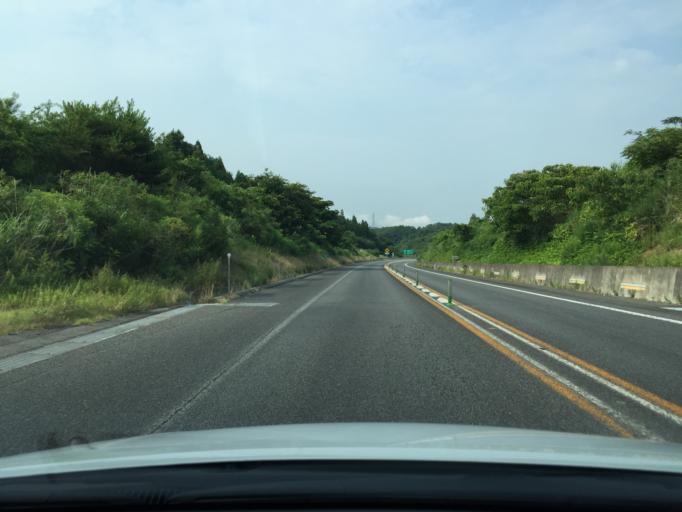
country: JP
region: Fukushima
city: Iwaki
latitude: 37.1013
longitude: 140.8735
